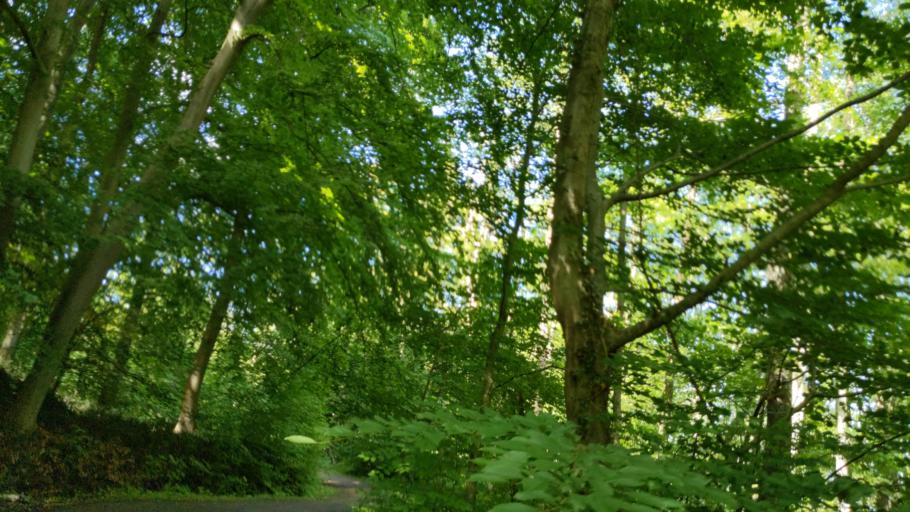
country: DE
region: Schleswig-Holstein
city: Schmilau
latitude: 53.6852
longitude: 10.7532
